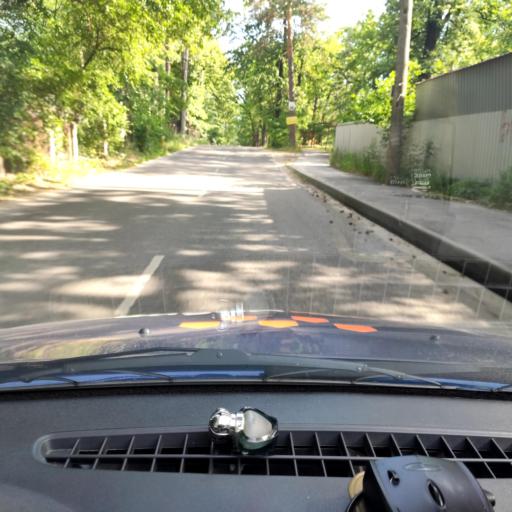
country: RU
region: Voronezj
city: Somovo
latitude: 51.7523
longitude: 39.3660
